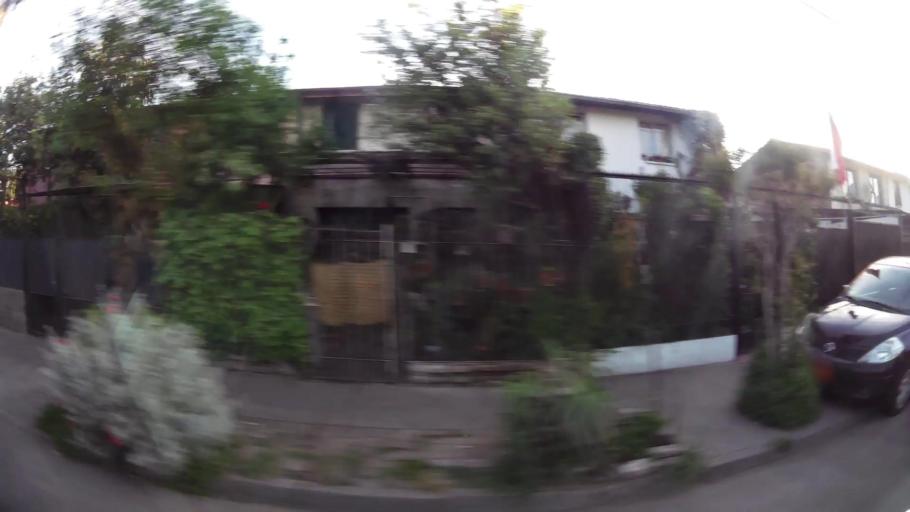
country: CL
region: Santiago Metropolitan
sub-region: Provincia de Santiago
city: Lo Prado
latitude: -33.4140
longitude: -70.6968
